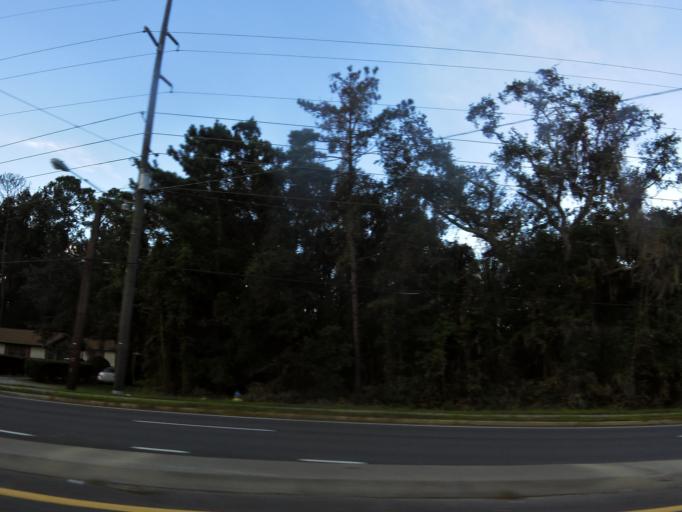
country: US
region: Georgia
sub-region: Camden County
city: St Marys
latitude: 30.7600
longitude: -81.6020
